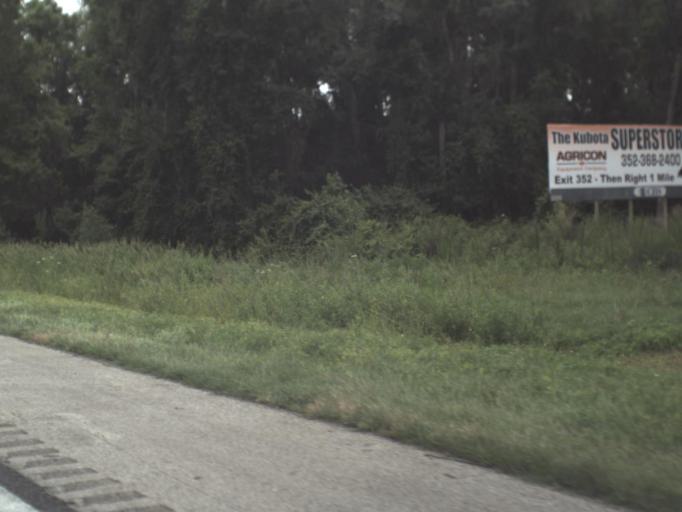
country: US
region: Florida
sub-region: Alachua County
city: Gainesville
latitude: 29.5343
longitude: -82.3217
